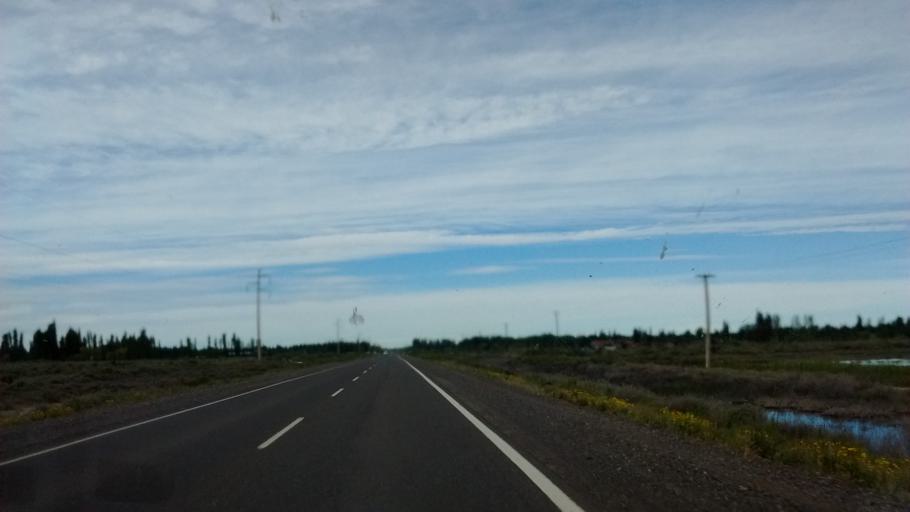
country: AR
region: Rio Negro
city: Contraalmirante Cordero
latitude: -38.6719
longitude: -68.1490
